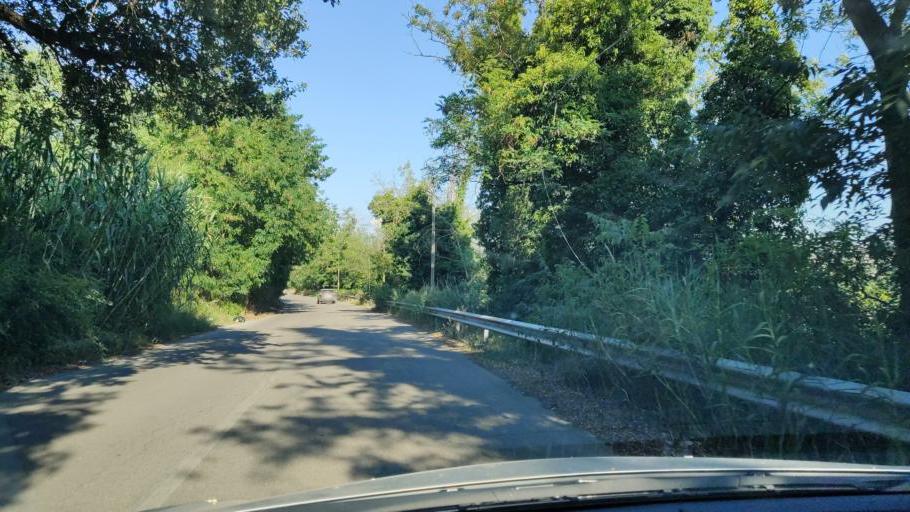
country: IT
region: Latium
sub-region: Provincia di Viterbo
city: Orte
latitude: 42.4695
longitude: 12.3760
